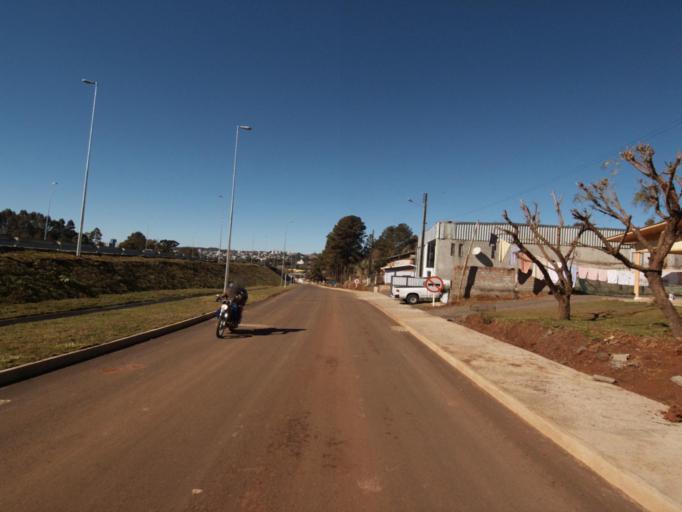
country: BR
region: Santa Catarina
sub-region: Xanxere
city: Xanxere
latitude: -26.8859
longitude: -52.4161
